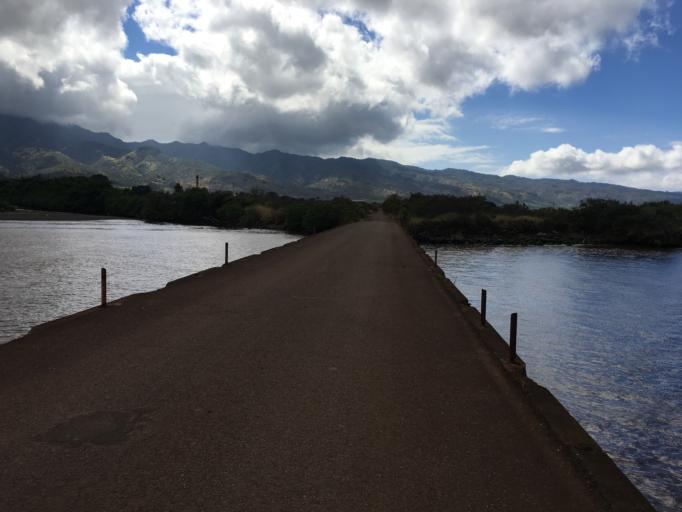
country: US
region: Hawaii
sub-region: Honolulu County
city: Hale'iwa
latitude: 21.5813
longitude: -158.1189
